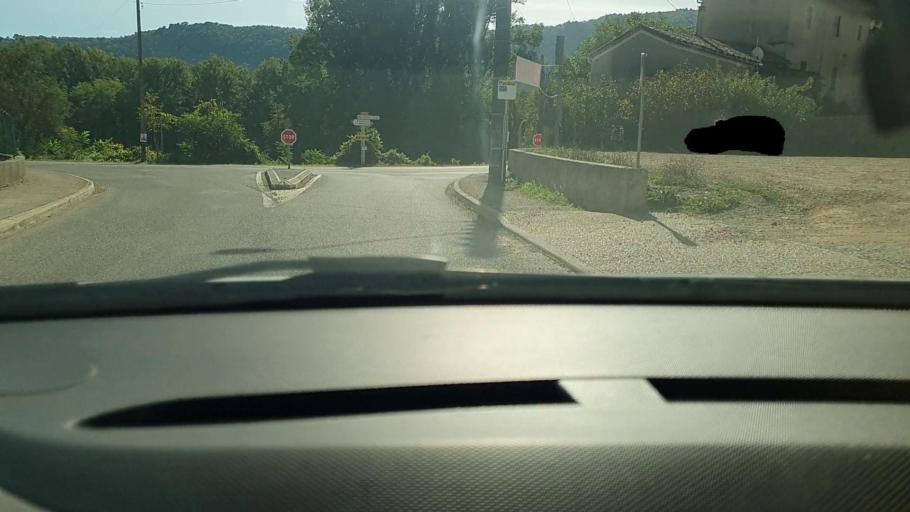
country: FR
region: Languedoc-Roussillon
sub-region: Departement du Gard
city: Molieres-sur-Ceze
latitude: 44.2663
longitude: 4.1499
